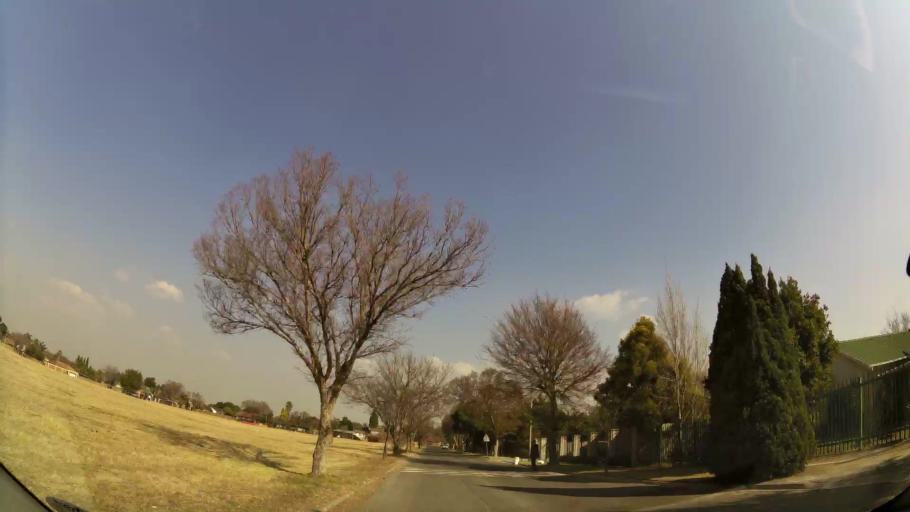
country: ZA
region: Gauteng
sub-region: Ekurhuleni Metropolitan Municipality
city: Benoni
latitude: -26.1545
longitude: 28.2802
